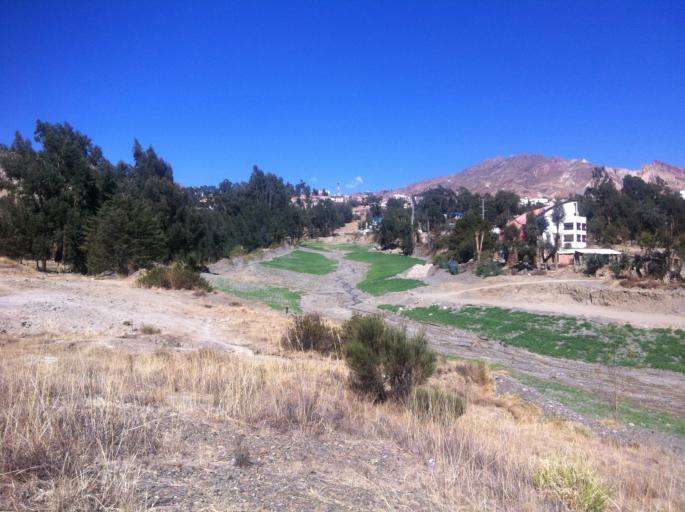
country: BO
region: La Paz
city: La Paz
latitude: -16.5364
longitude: -68.0670
